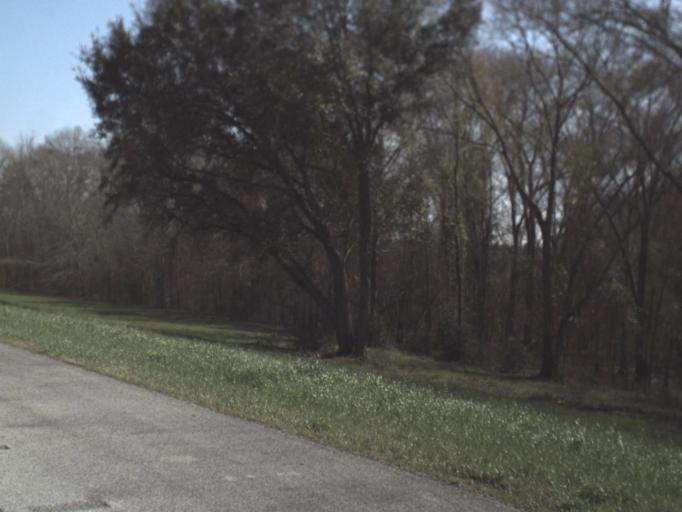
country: US
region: Florida
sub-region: Jackson County
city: Marianna
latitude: 30.6851
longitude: -85.1081
